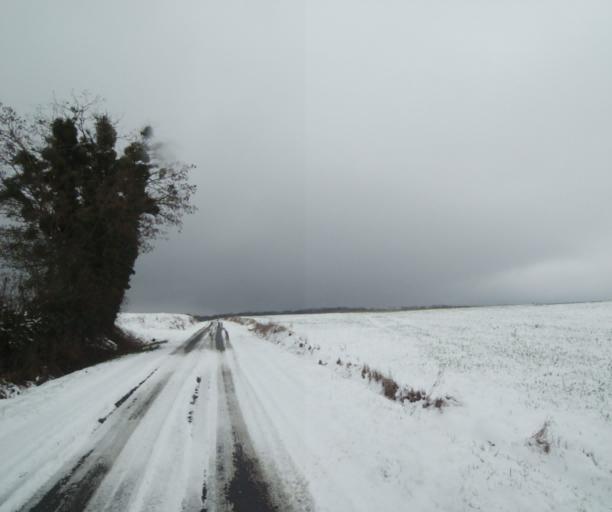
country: FR
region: Champagne-Ardenne
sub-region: Departement de la Haute-Marne
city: Wassy
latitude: 48.4704
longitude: 4.9637
